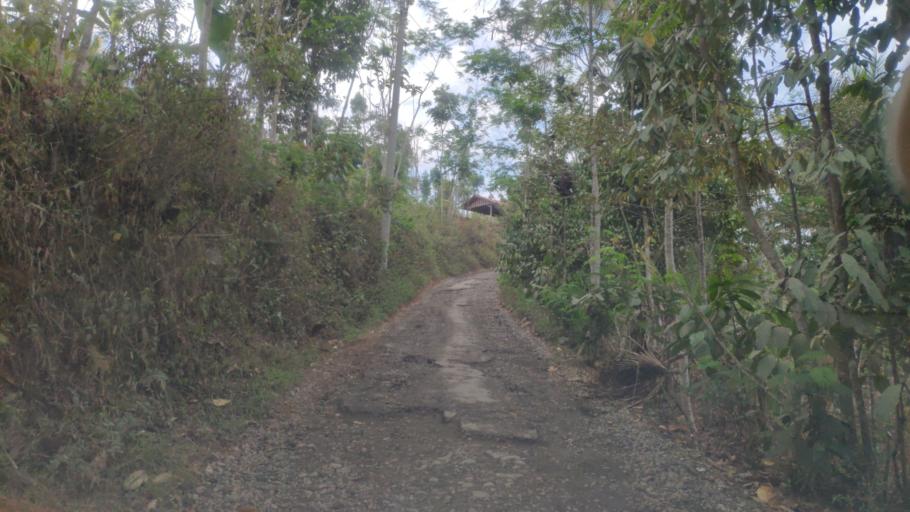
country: ID
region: Central Java
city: Wonosobo
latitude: -7.4470
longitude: 109.8271
